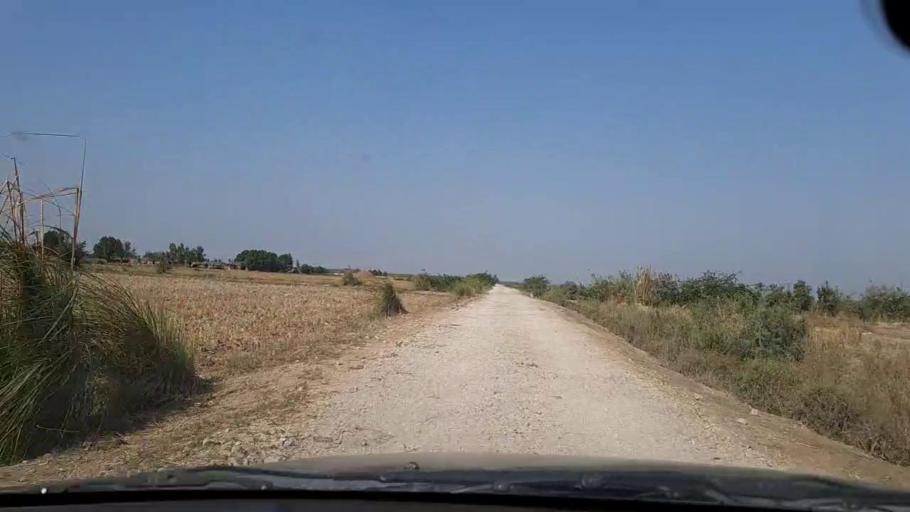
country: PK
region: Sindh
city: Mirpur Sakro
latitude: 24.3733
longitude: 67.6830
